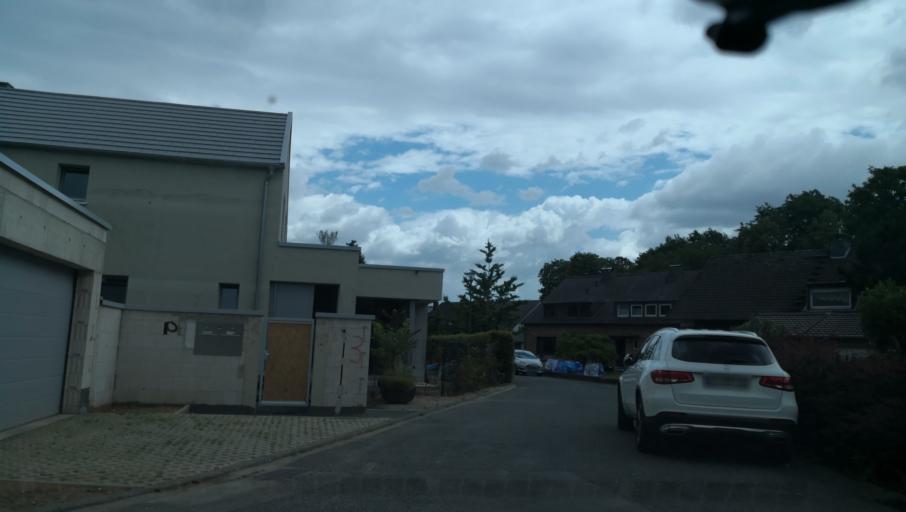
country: DE
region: North Rhine-Westphalia
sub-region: Regierungsbezirk Koln
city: Mengenich
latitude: 50.9531
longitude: 6.8749
